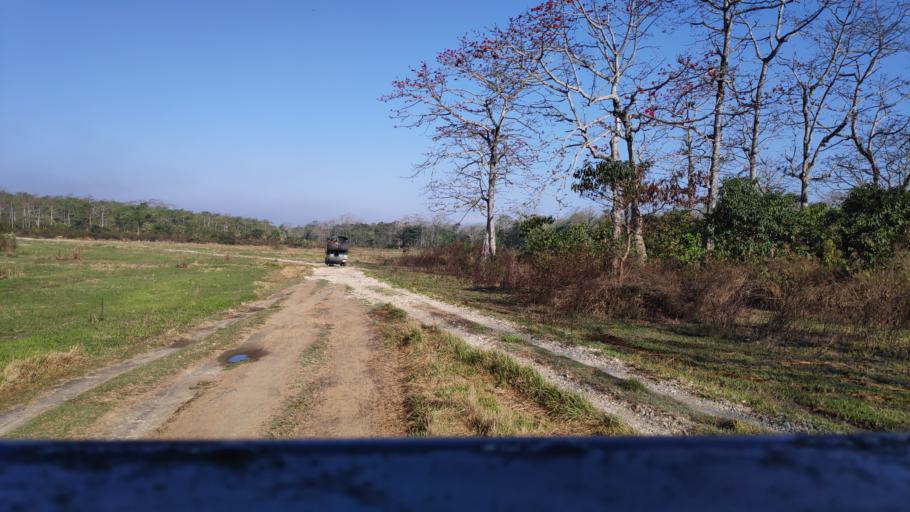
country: NP
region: Central Region
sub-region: Narayani Zone
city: Bharatpur
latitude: 27.5600
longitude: 84.5240
